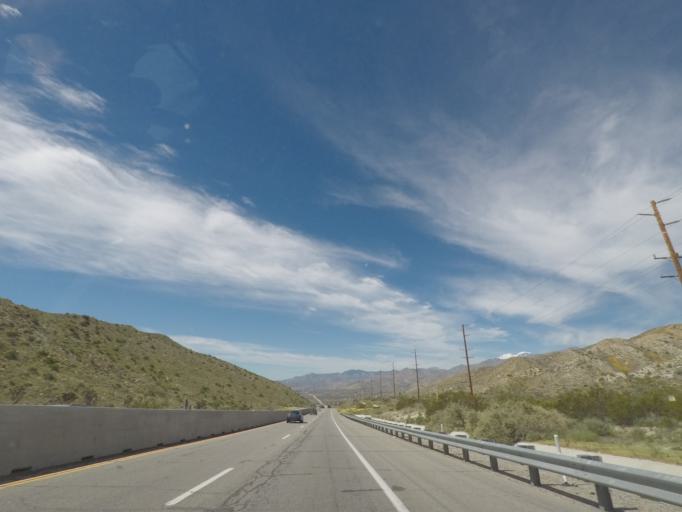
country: US
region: California
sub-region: San Bernardino County
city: Yucca Valley
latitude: 34.1074
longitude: -116.4850
